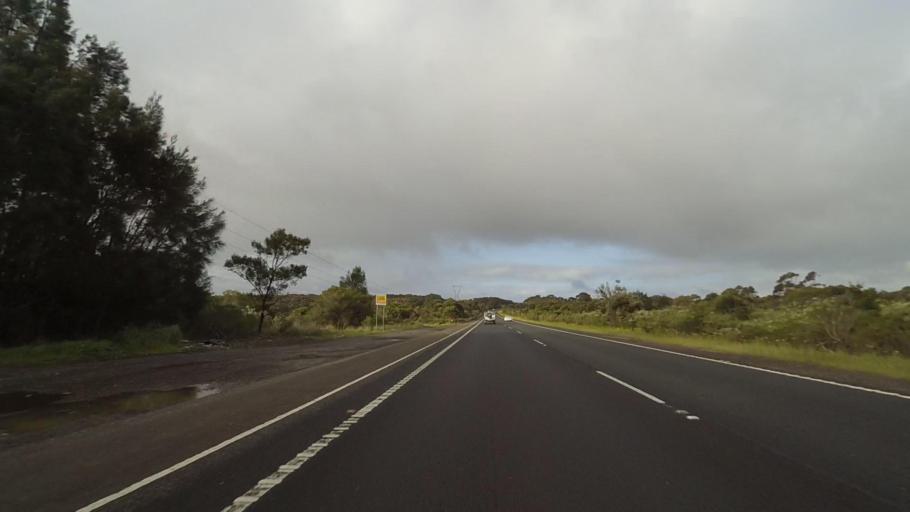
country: AU
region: New South Wales
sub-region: Wollongong
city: Bulli
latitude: -34.2527
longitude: 150.9336
